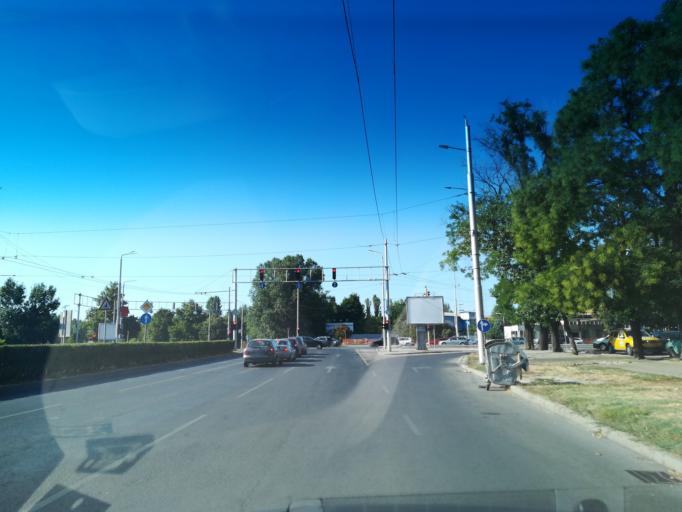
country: BG
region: Plovdiv
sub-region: Obshtina Plovdiv
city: Plovdiv
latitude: 42.1608
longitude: 24.7302
